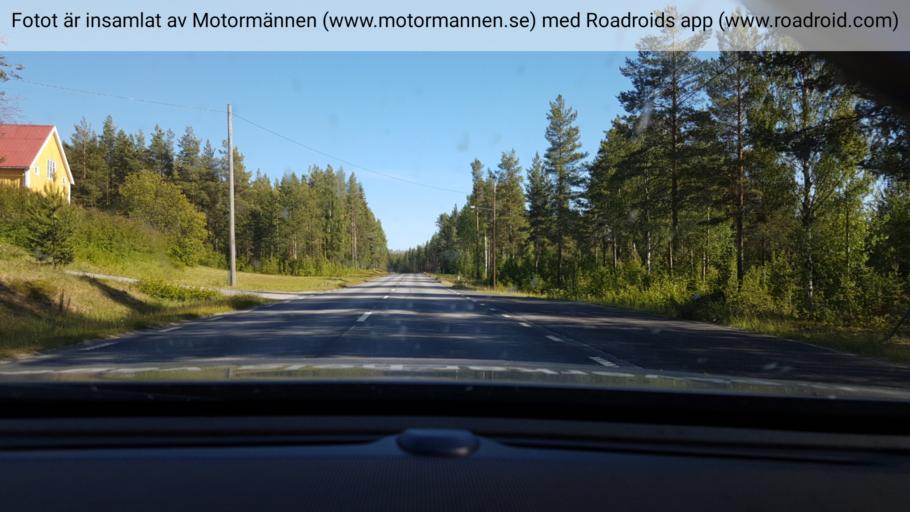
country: SE
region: Vaesterbotten
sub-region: Lycksele Kommun
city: Lycksele
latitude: 64.5364
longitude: 18.7593
